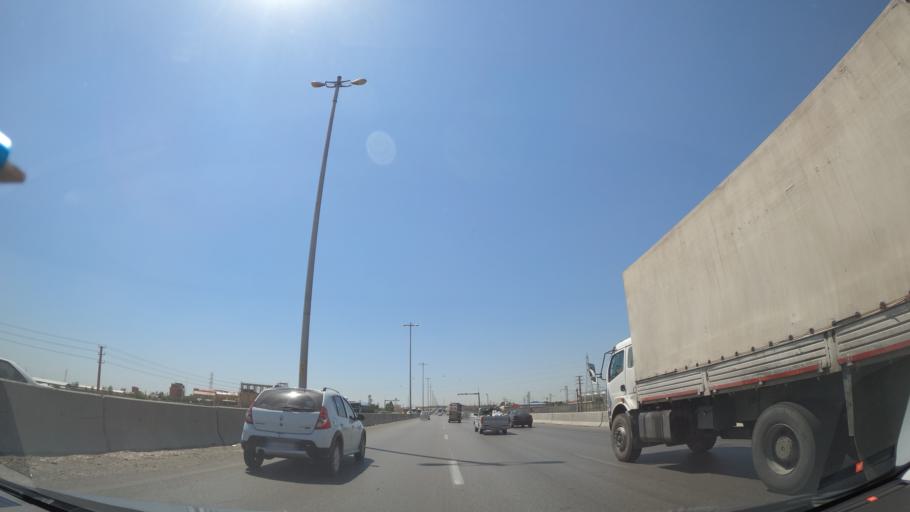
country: IR
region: Alborz
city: Karaj
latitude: 35.9060
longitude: 50.8451
